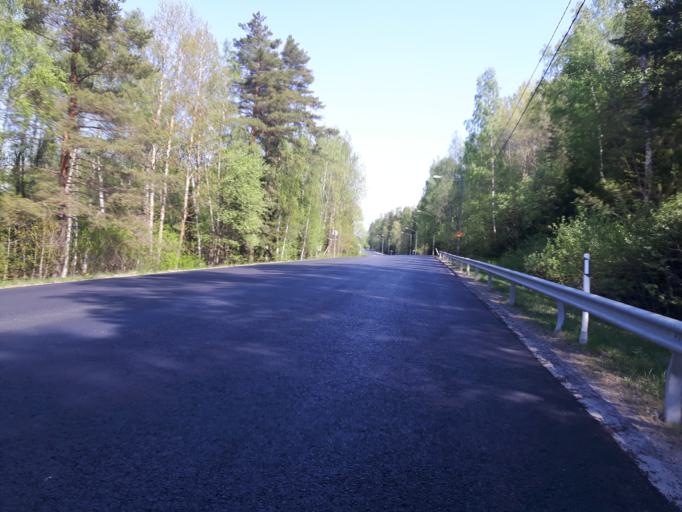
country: FI
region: Uusimaa
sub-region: Helsinki
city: Pornainen
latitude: 60.3350
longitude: 25.4587
